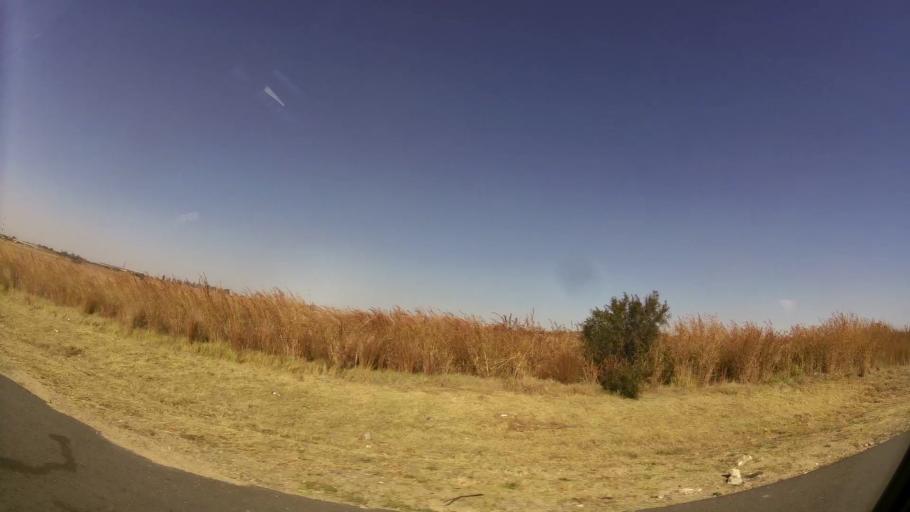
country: ZA
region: Gauteng
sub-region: City of Johannesburg Metropolitan Municipality
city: Diepsloot
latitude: -25.9813
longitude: 27.9291
